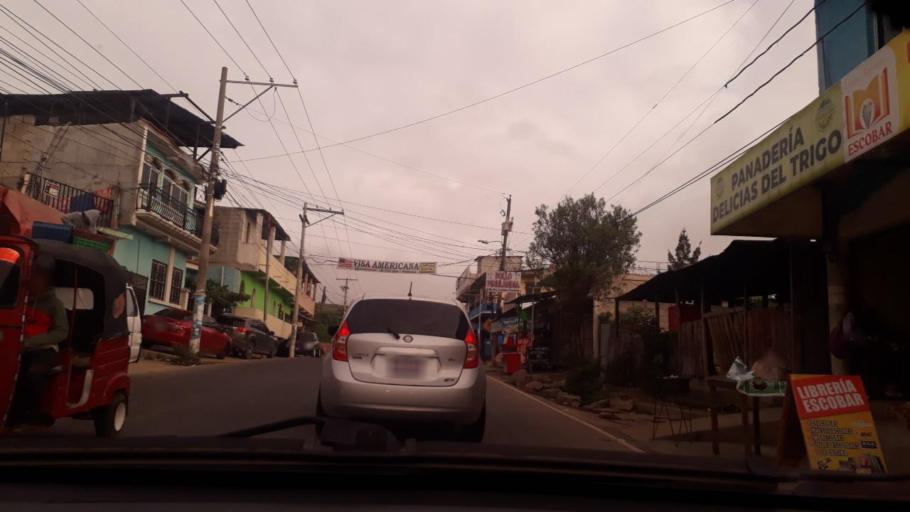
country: GT
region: Jalapa
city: Jalapa
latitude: 14.6488
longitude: -89.9980
